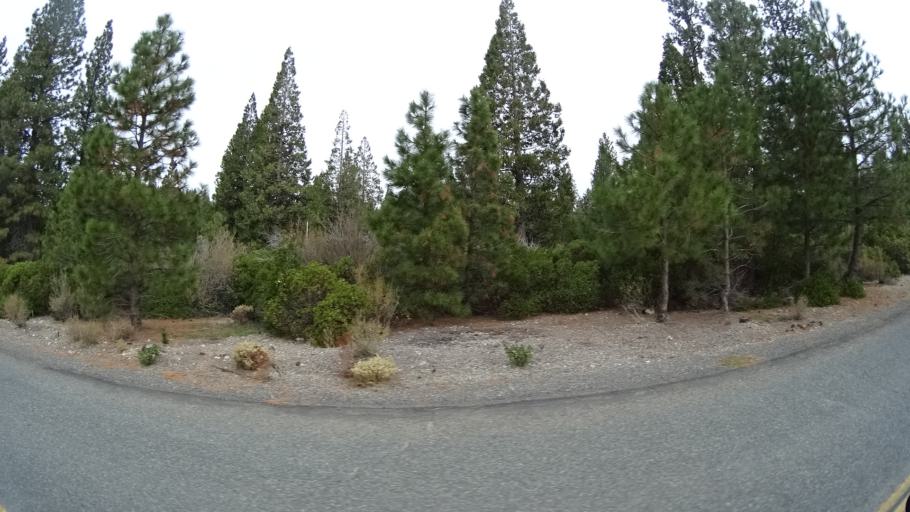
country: US
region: California
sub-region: Siskiyou County
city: Weed
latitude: 41.4105
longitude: -122.3705
